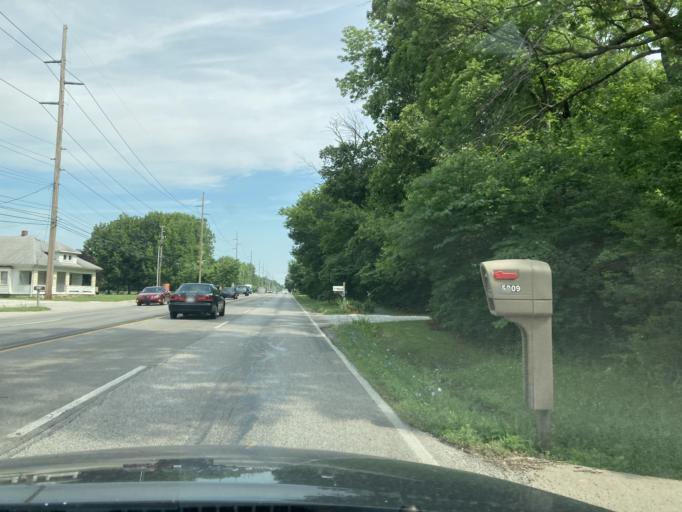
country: US
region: Indiana
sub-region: Marion County
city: Broad Ripple
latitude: 39.8468
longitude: -86.1913
